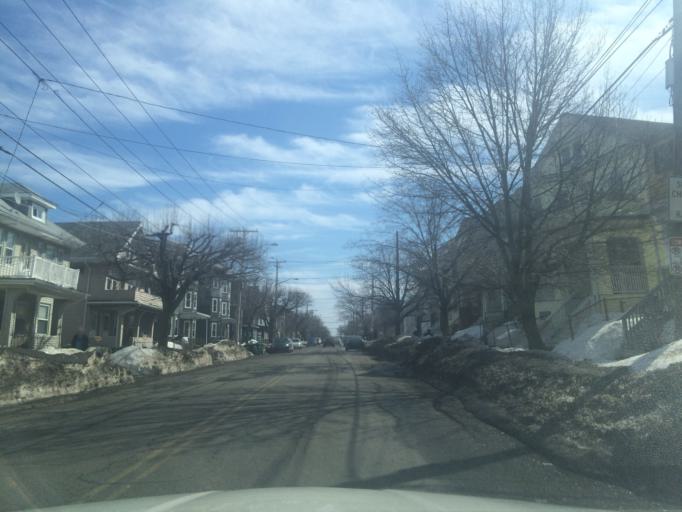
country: US
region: Massachusetts
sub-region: Middlesex County
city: Medford
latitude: 42.4138
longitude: -71.1252
